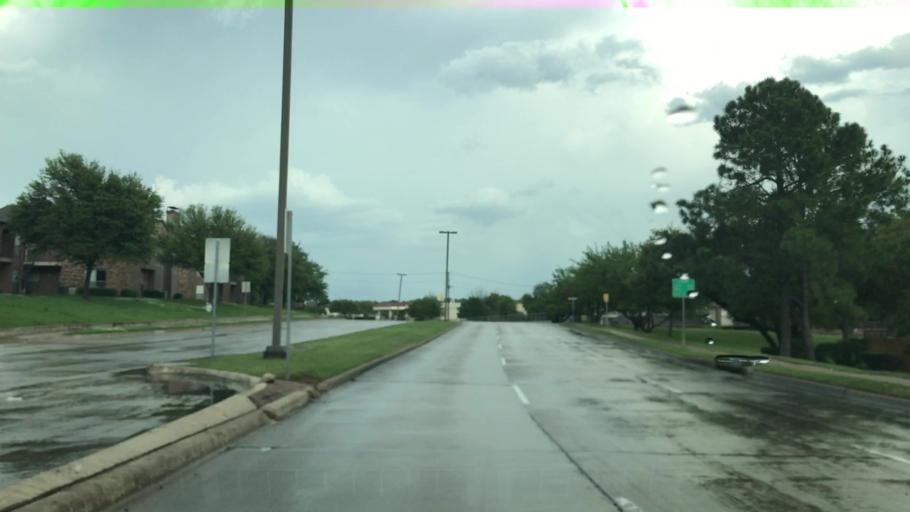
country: US
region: Texas
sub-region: Dallas County
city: Irving
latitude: 32.8669
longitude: -96.9802
